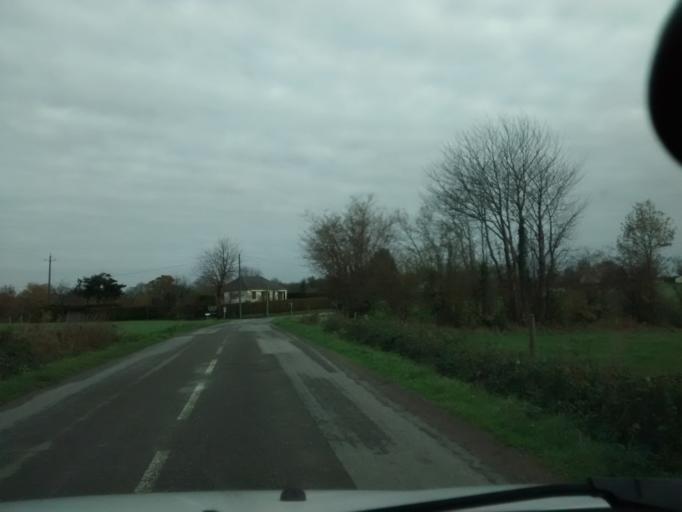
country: FR
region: Brittany
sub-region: Departement d'Ille-et-Vilaine
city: Erbree
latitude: 48.1128
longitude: -1.1246
